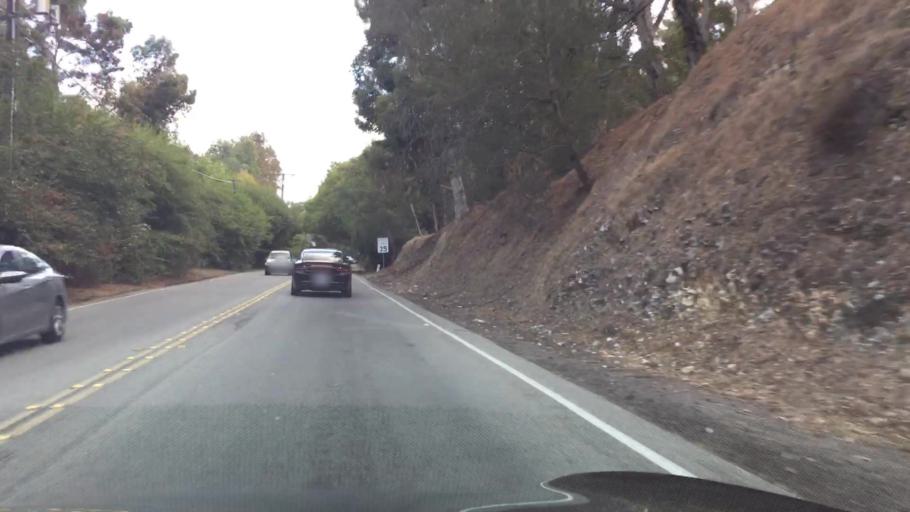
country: US
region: California
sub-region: Los Angeles County
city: La Habra Heights
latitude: 33.9711
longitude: -117.9652
